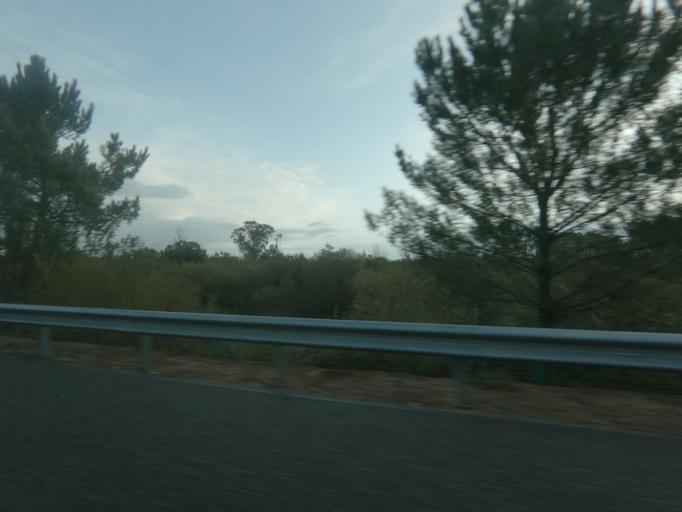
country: ES
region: Galicia
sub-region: Provincia de Pontevedra
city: Tui
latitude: 42.0860
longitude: -8.6397
